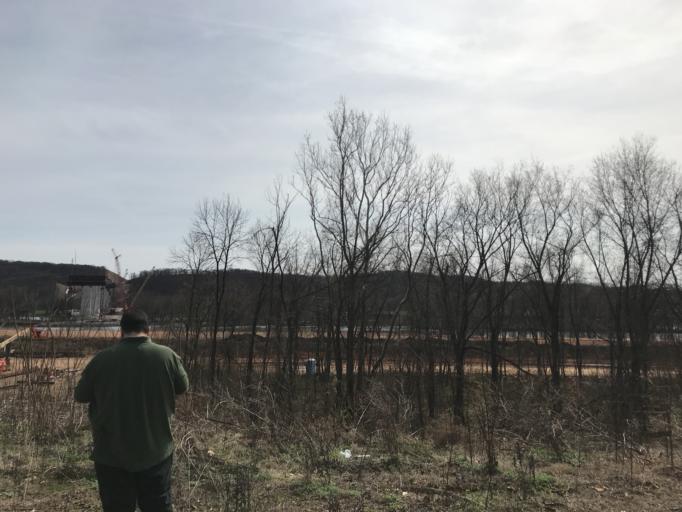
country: US
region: Pennsylvania
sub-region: Northumberland County
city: Northumberland
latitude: 40.9097
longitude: -76.8368
